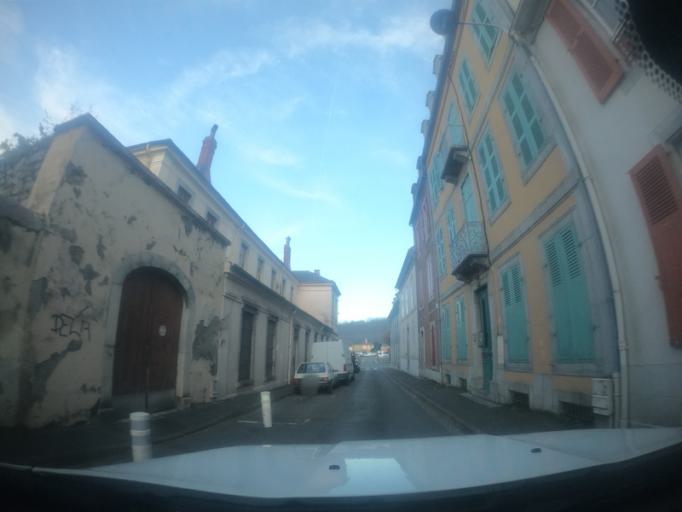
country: FR
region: Midi-Pyrenees
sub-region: Departement des Hautes-Pyrenees
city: Bagneres-de-Bigorre
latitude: 43.0644
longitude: 0.1522
